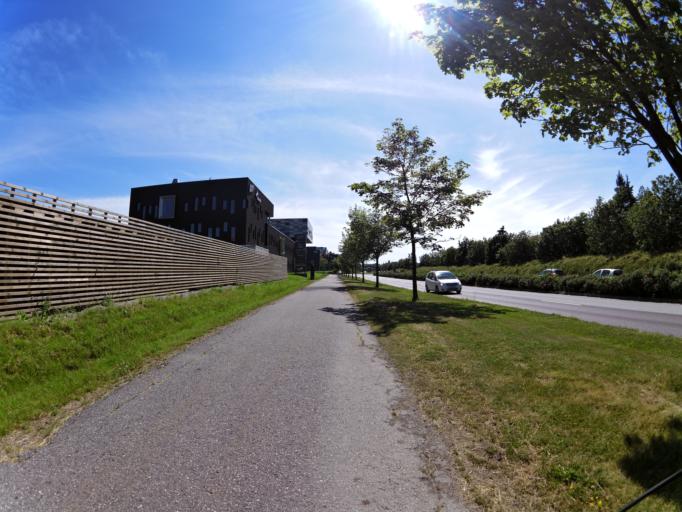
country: NO
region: Ostfold
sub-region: Fredrikstad
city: Fredrikstad
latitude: 59.2245
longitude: 10.9531
